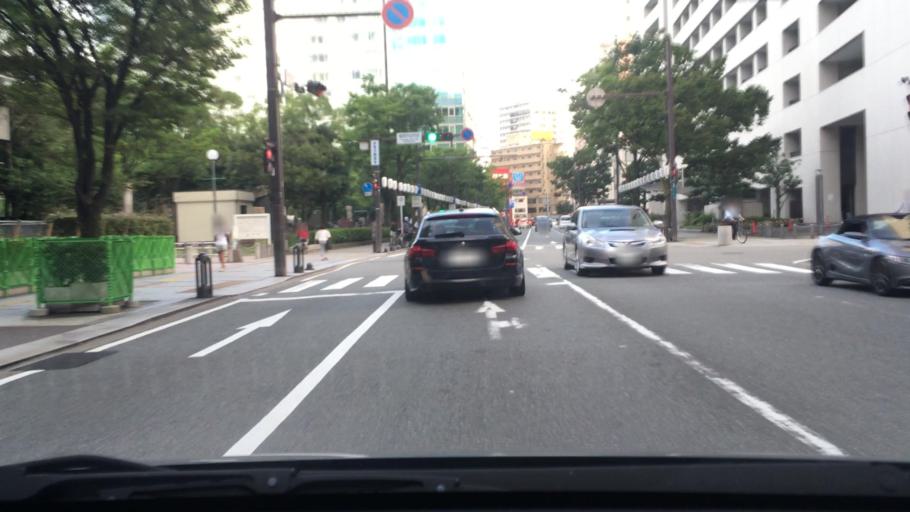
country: JP
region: Fukuoka
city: Fukuoka-shi
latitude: 33.5911
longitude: 130.4018
